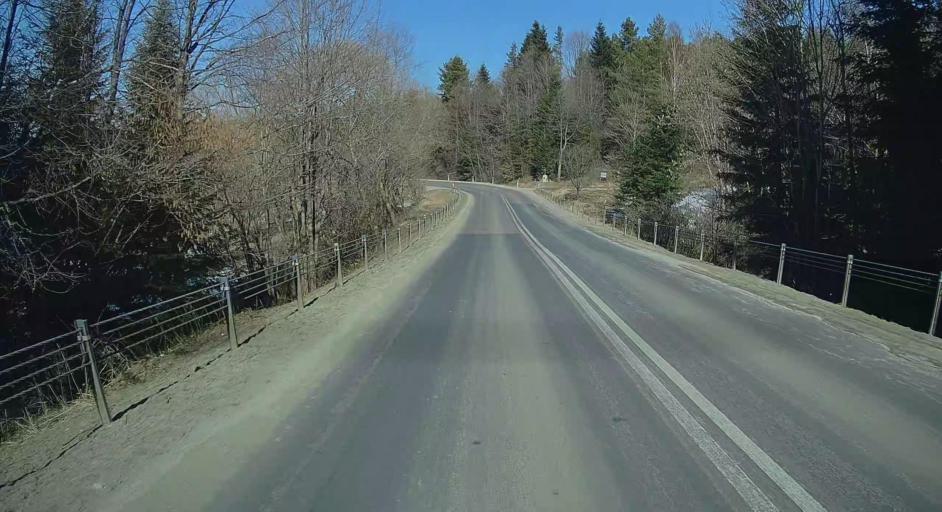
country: PL
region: Subcarpathian Voivodeship
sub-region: Powiat bieszczadzki
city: Ustrzyki Dolne
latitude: 49.5236
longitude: 22.6041
